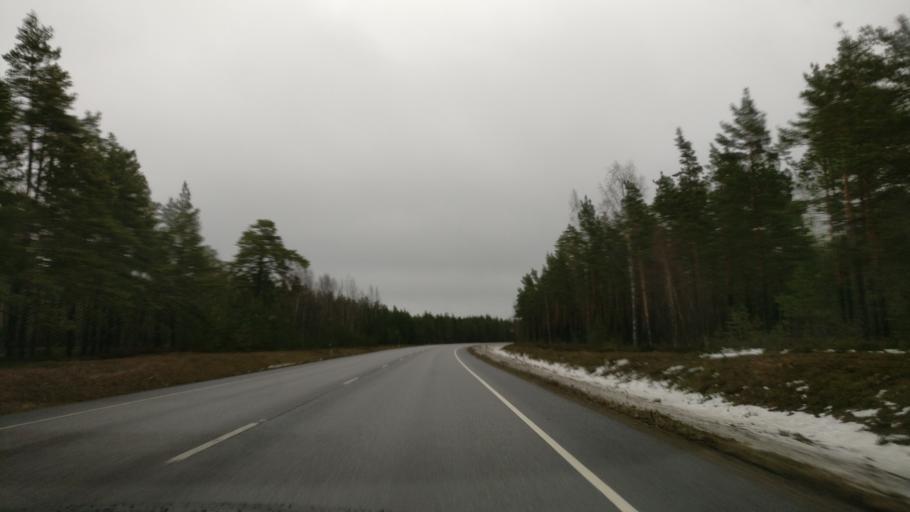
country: FI
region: Uusimaa
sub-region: Raaseporin
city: Hanko
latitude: 59.8587
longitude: 23.0293
